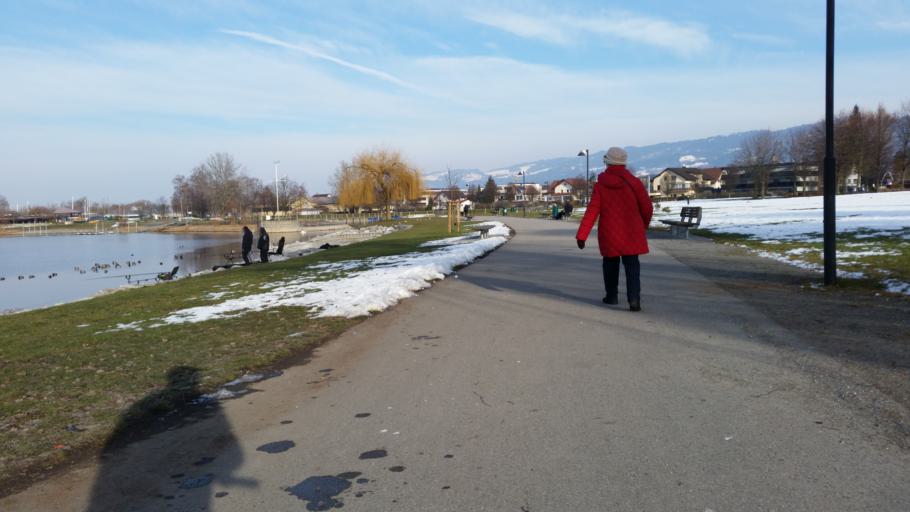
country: AT
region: Vorarlberg
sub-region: Politischer Bezirk Bregenz
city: Hard
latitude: 47.4922
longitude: 9.6855
